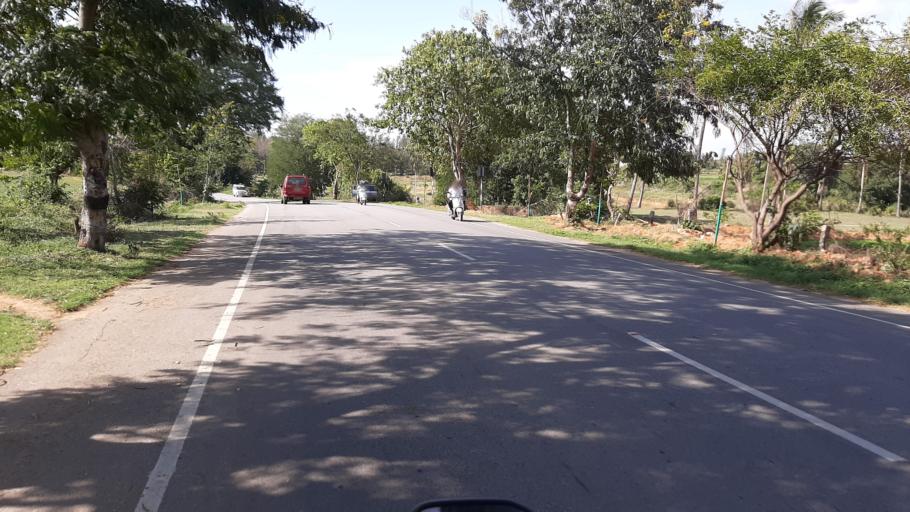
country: IN
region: Tamil Nadu
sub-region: Krishnagiri
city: Denkanikota
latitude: 12.5430
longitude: 77.7885
